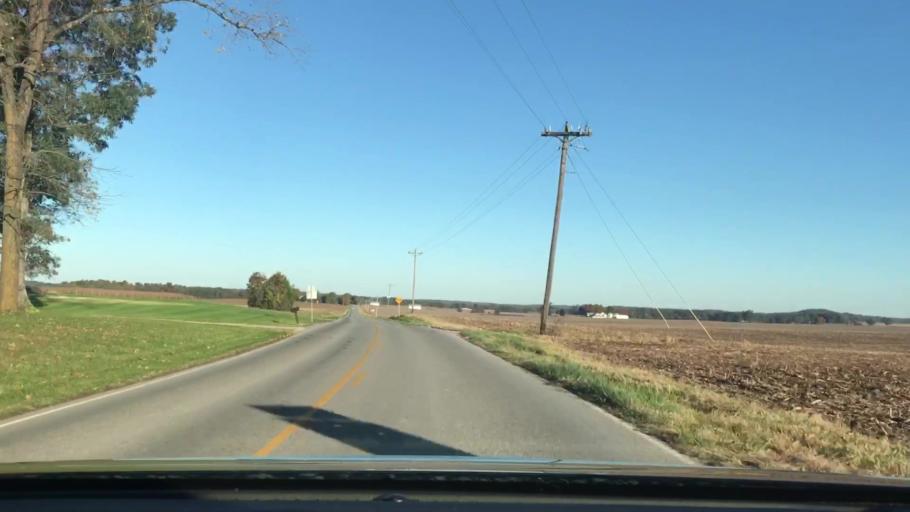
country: US
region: Kentucky
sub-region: Logan County
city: Auburn
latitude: 36.8318
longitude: -86.6844
